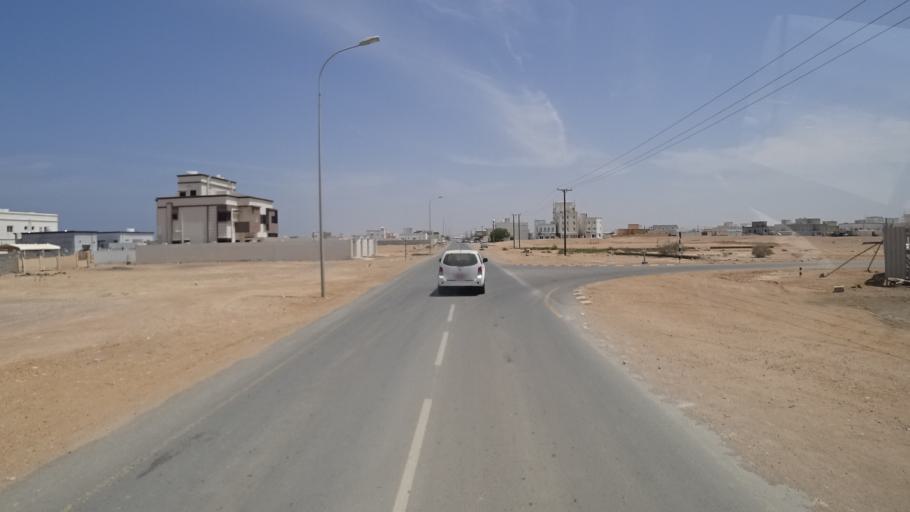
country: OM
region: Ash Sharqiyah
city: Sur
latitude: 22.6169
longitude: 59.4603
